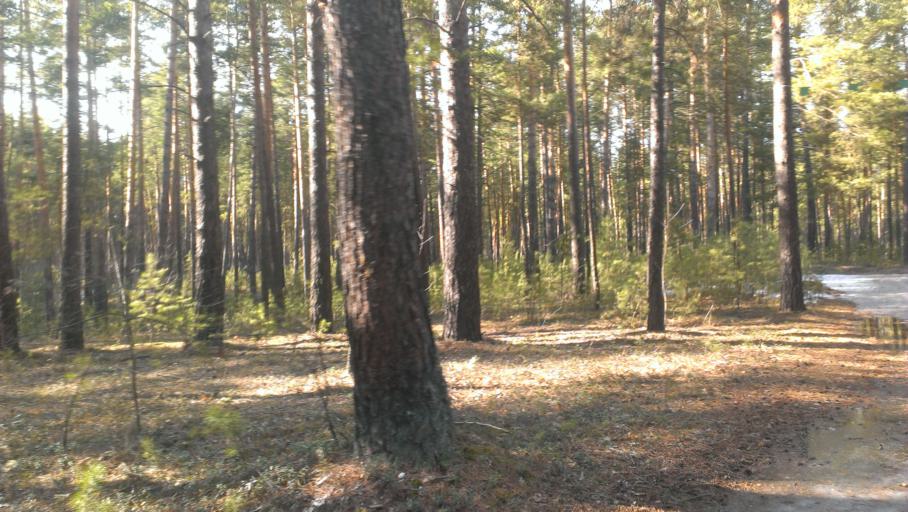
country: RU
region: Altai Krai
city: Yuzhnyy
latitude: 53.2838
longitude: 83.6992
